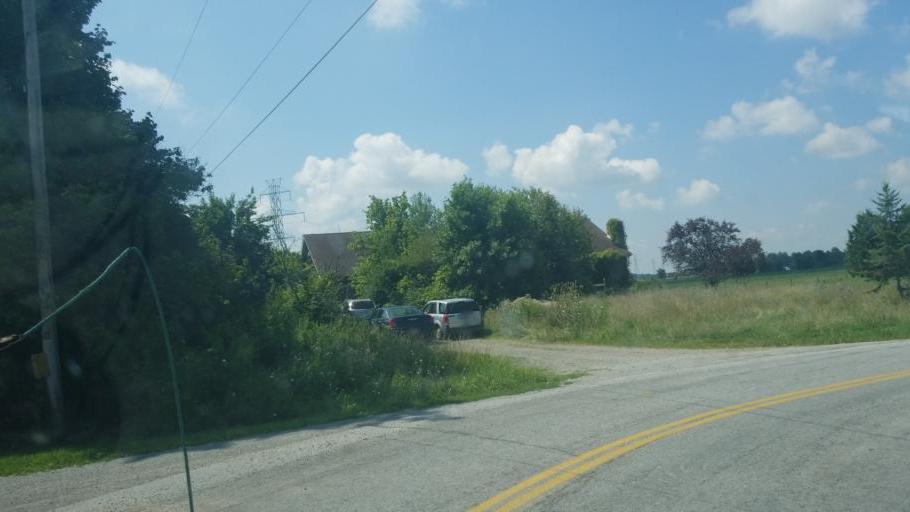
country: US
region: Ohio
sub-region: Allen County
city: Lima
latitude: 40.6990
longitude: -83.9614
